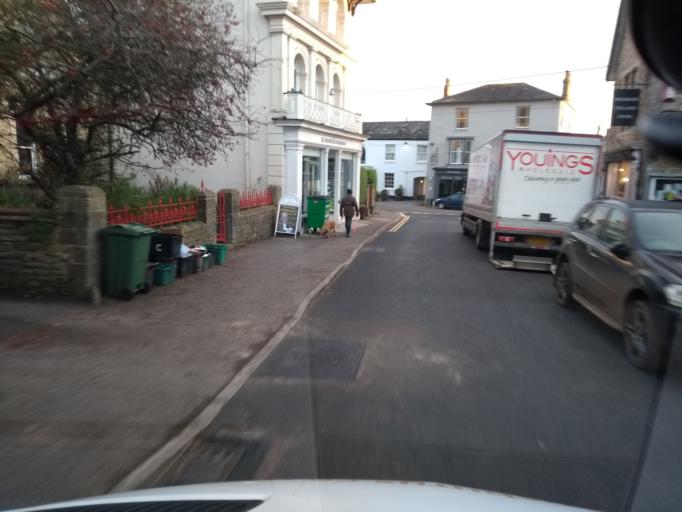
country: GB
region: England
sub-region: Somerset
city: Wedmore
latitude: 51.2279
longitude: -2.8095
